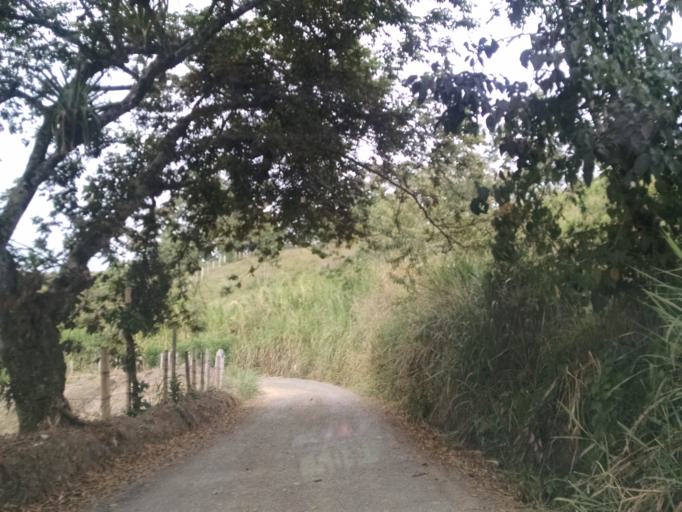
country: CO
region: Valle del Cauca
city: Ulloa
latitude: 4.7199
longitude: -75.7334
